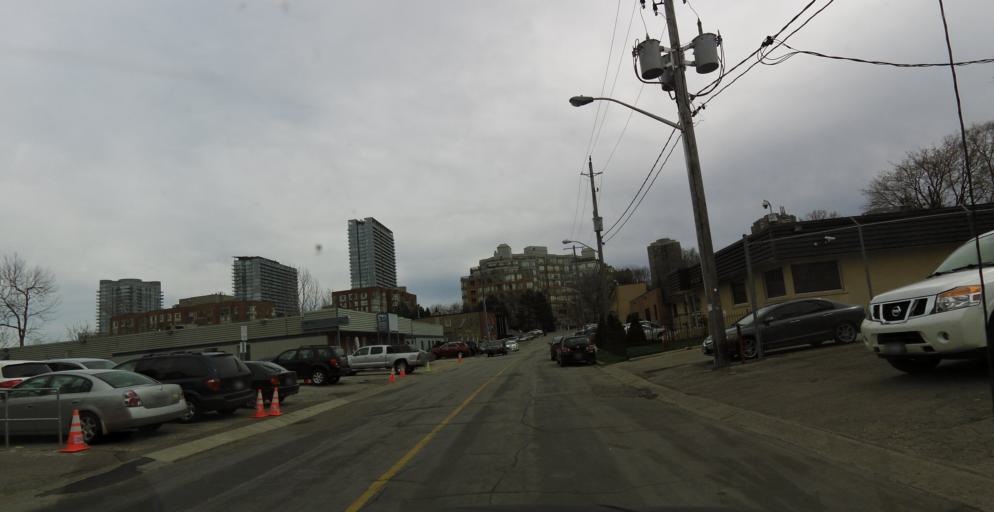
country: CA
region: Ontario
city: Toronto
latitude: 43.6383
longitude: -79.4754
